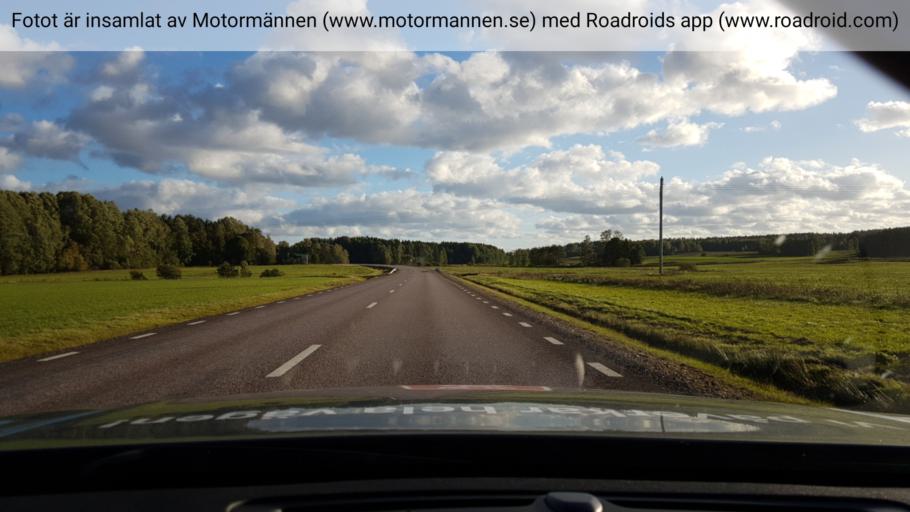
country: SE
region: Vaermland
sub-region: Karlstads Kommun
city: Molkom
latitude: 59.6209
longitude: 13.7298
